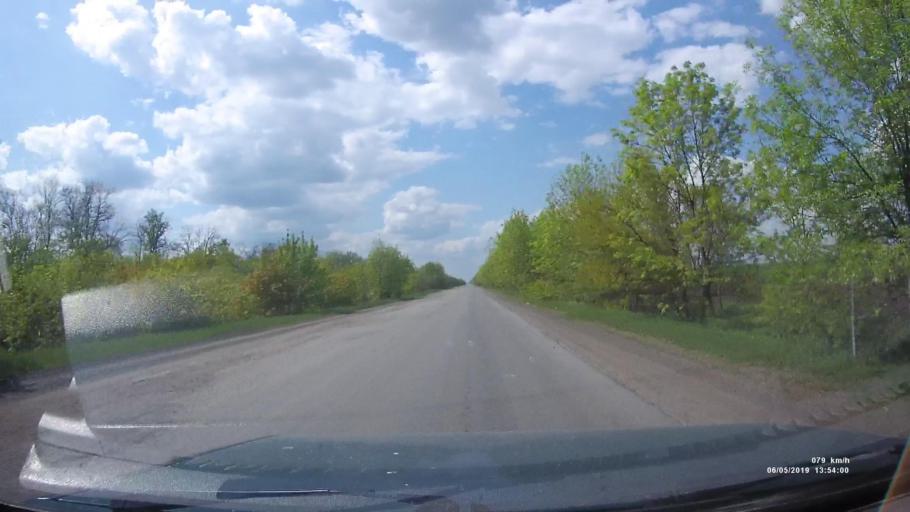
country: RU
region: Rostov
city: Melikhovskaya
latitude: 47.6719
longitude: 40.4536
